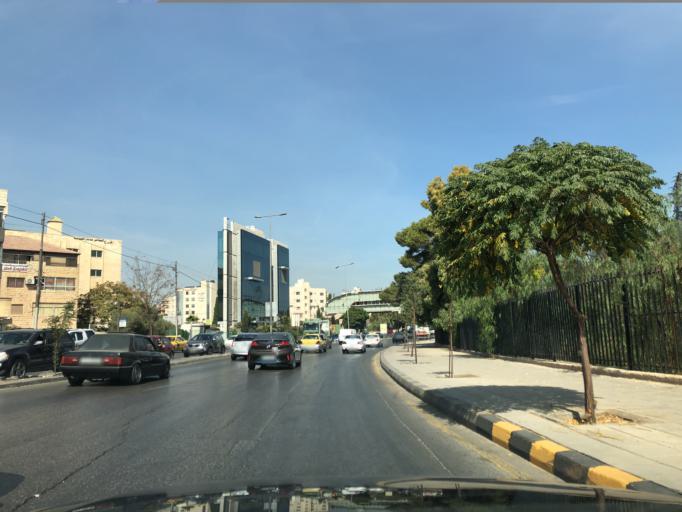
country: JO
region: Amman
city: Amman
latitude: 31.9780
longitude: 35.9034
